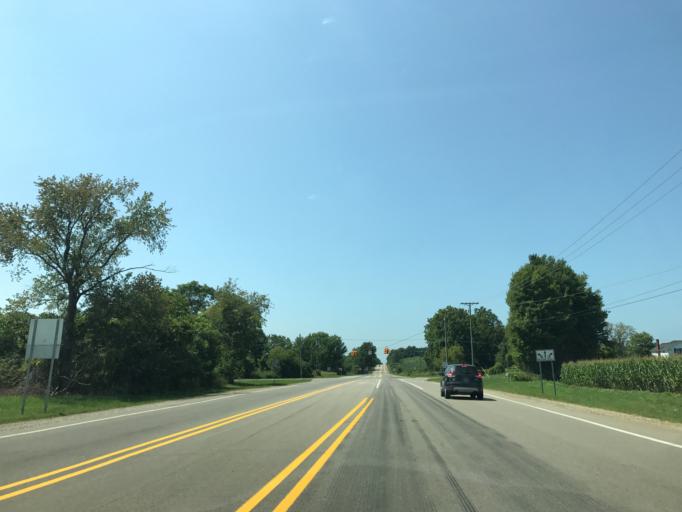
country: US
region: Michigan
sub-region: Berrien County
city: Buchanan
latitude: 41.8051
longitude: -86.3567
